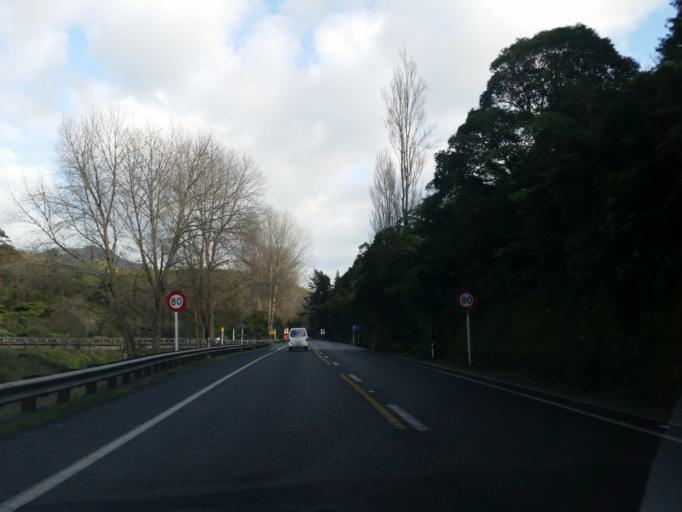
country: NZ
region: Waikato
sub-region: Hauraki District
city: Waihi
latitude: -37.4170
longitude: 175.7656
